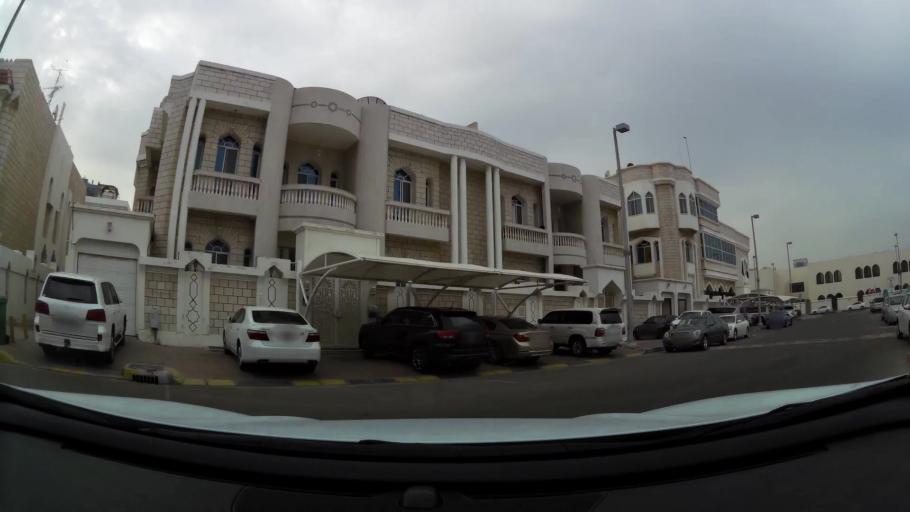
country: AE
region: Abu Dhabi
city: Abu Dhabi
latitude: 24.4830
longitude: 54.3701
